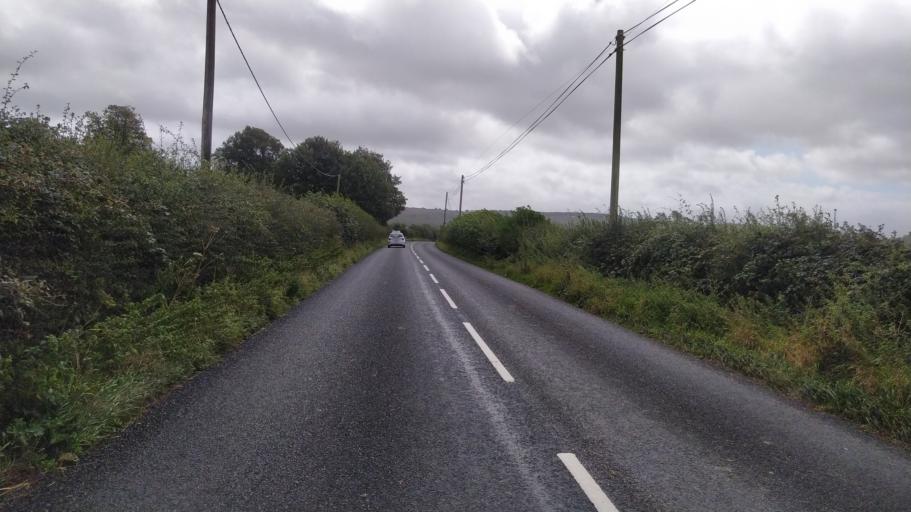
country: GB
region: England
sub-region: Dorset
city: Shaftesbury
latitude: 50.9942
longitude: -2.1735
